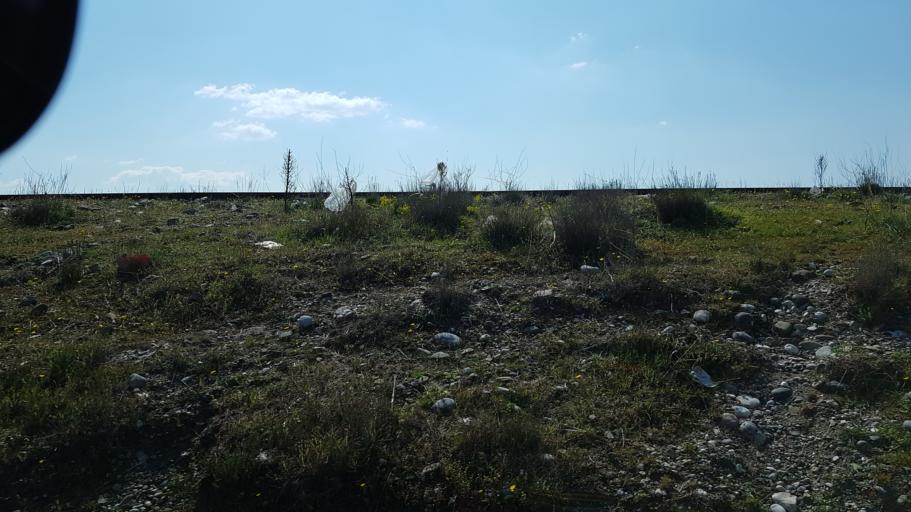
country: AL
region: Shkoder
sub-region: Rrethi i Shkodres
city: Vau i Dejes
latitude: 41.9989
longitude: 19.6078
